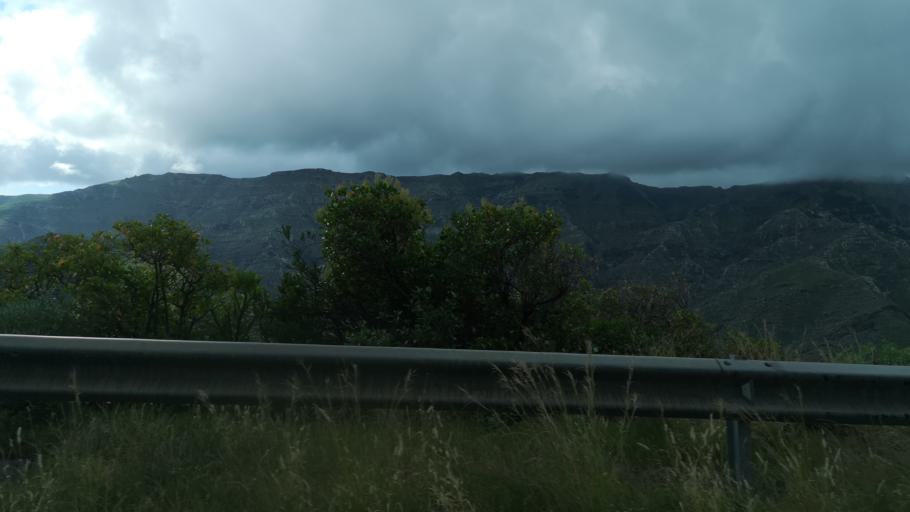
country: ES
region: Canary Islands
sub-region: Provincia de Santa Cruz de Tenerife
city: San Sebastian de la Gomera
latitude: 28.1232
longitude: -17.1556
